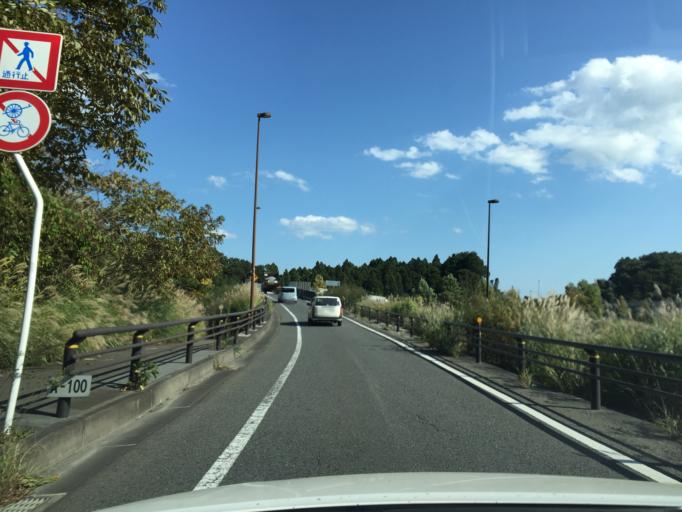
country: JP
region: Fukushima
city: Iwaki
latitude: 37.0205
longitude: 140.8924
